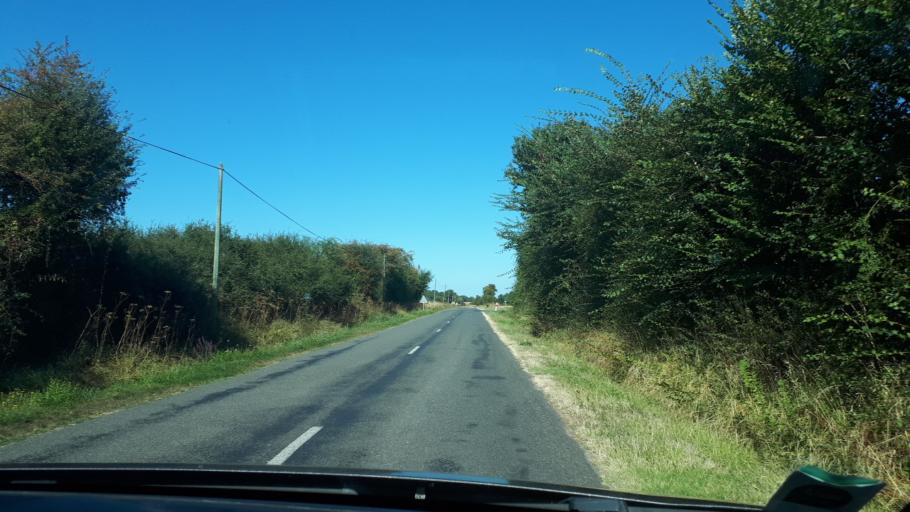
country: FR
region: Centre
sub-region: Departement du Loiret
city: Briare
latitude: 47.5910
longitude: 2.7230
